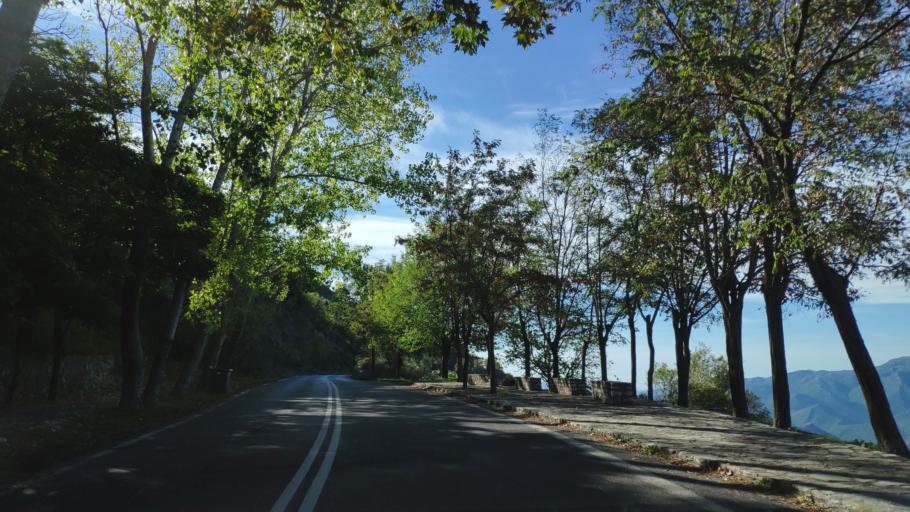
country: GR
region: Peloponnese
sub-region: Nomos Arkadias
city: Dimitsana
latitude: 37.5604
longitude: 22.0628
